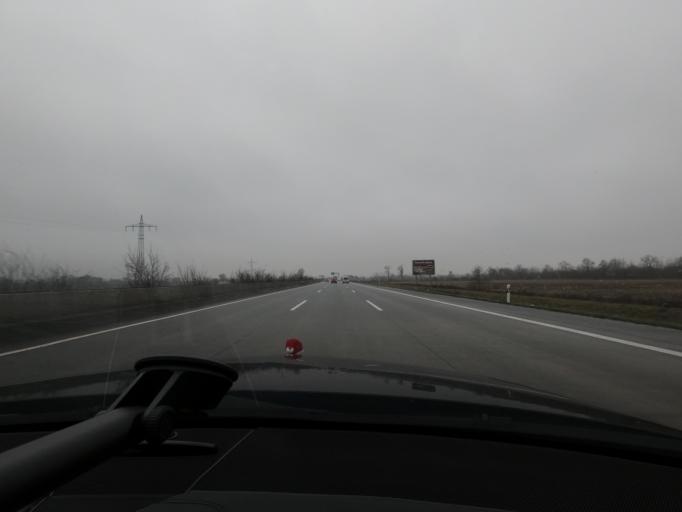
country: DE
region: Schleswig-Holstein
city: Wasbek
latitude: 54.0864
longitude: 9.9277
